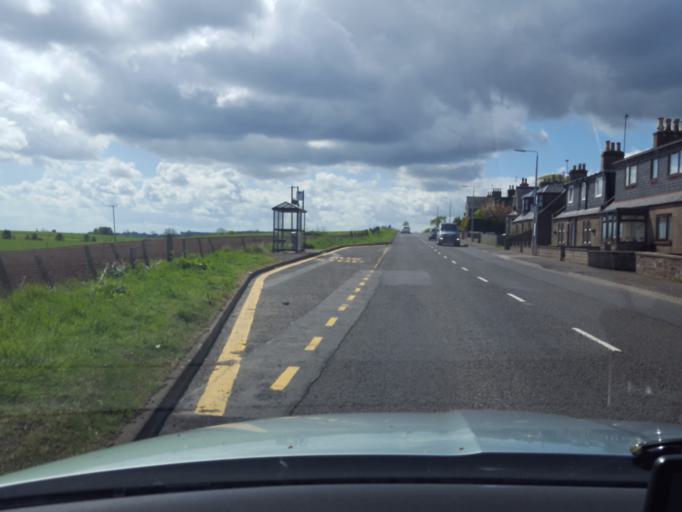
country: GB
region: Scotland
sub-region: Angus
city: Brechin
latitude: 56.7489
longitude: -2.6459
